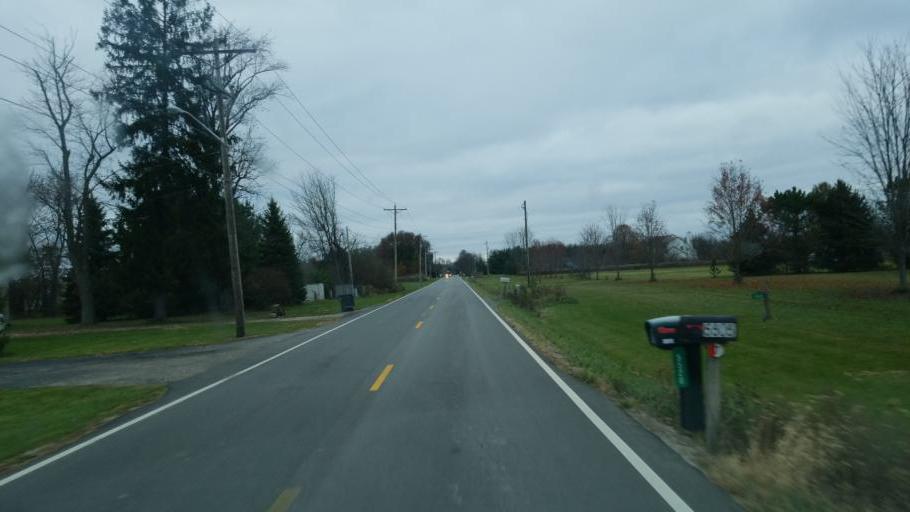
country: US
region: Ohio
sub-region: Delaware County
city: Sunbury
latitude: 40.1623
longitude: -82.8408
